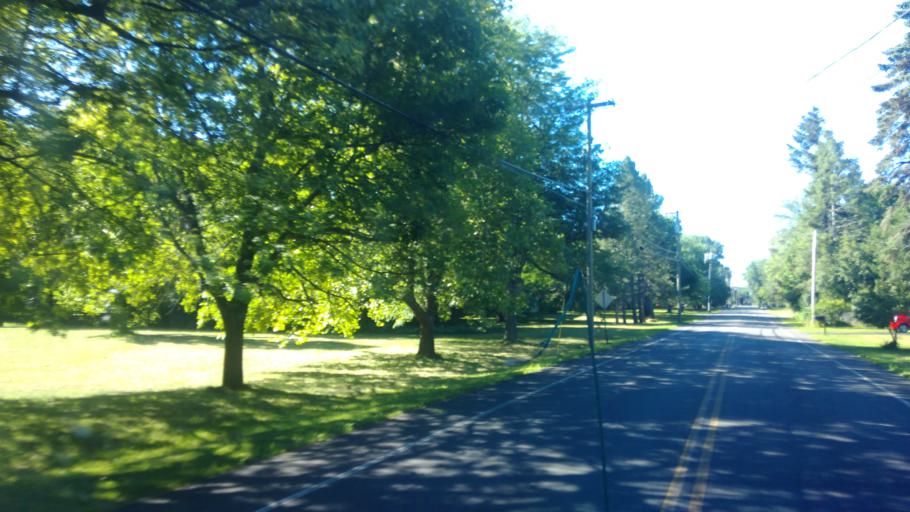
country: US
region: New York
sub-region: Monroe County
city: Webster
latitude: 43.2373
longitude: -77.4615
